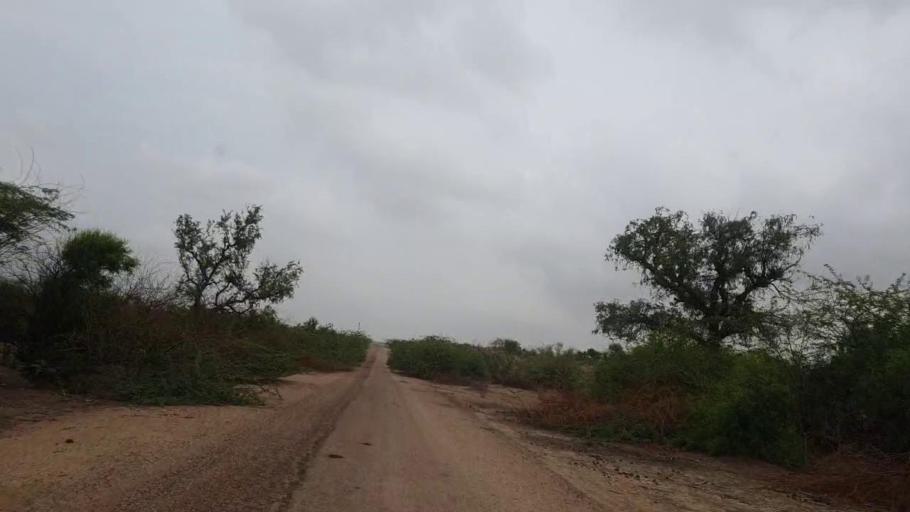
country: PK
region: Sindh
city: Diplo
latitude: 24.5196
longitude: 69.4701
